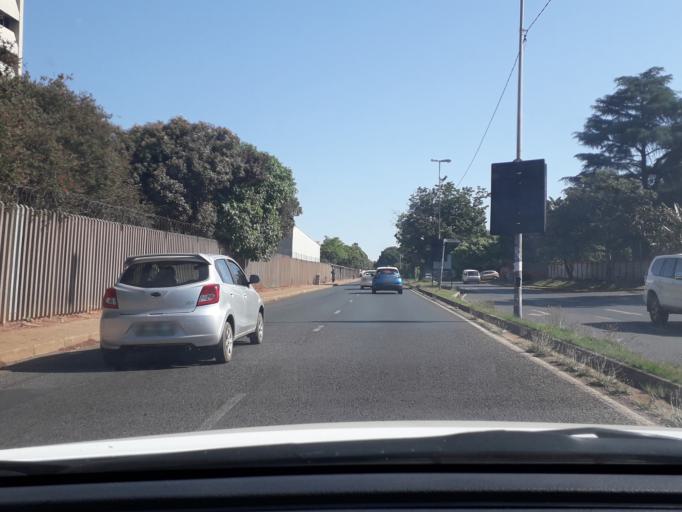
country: ZA
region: Gauteng
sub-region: City of Johannesburg Metropolitan Municipality
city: Johannesburg
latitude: -26.1208
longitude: 27.9737
